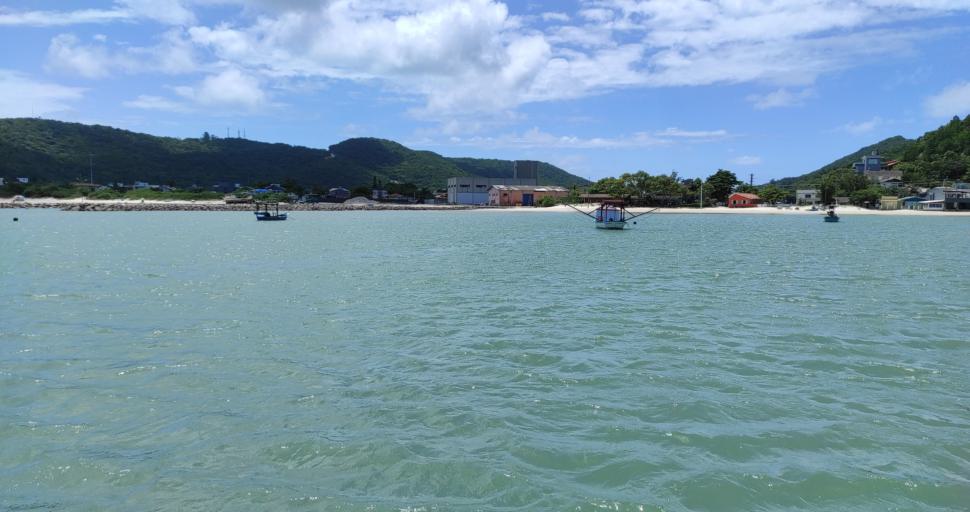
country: BR
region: Santa Catarina
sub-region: Porto Belo
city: Porto Belo
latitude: -27.1829
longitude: -48.5247
